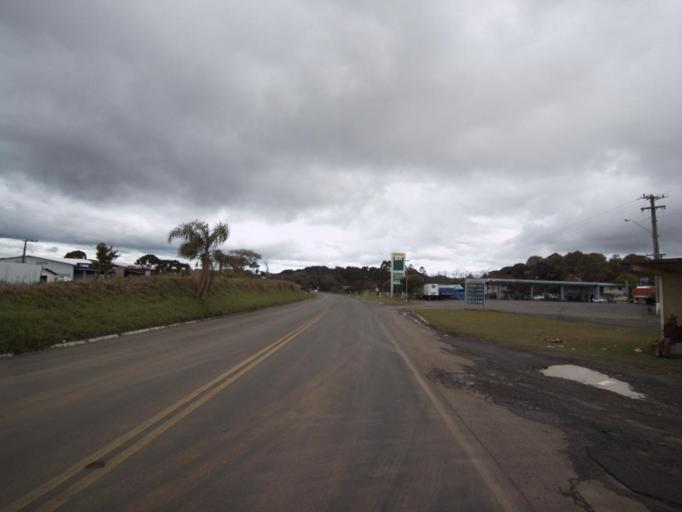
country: BR
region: Santa Catarina
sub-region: Concordia
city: Concordia
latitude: -27.2452
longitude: -51.9522
